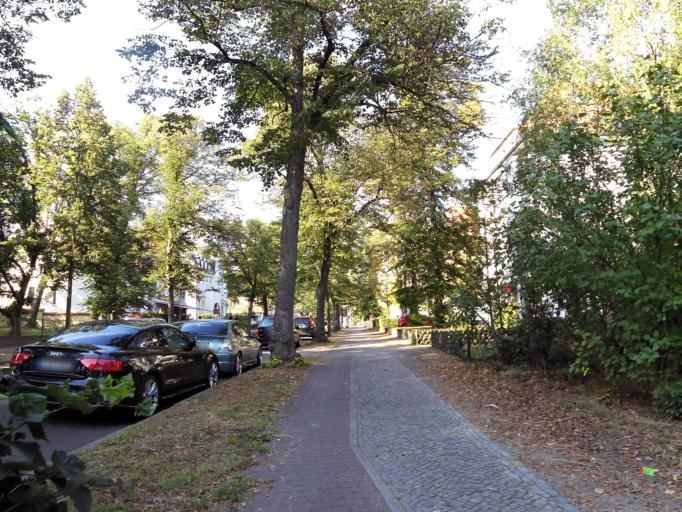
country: DE
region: Berlin
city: Nikolassee
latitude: 52.4372
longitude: 13.2162
